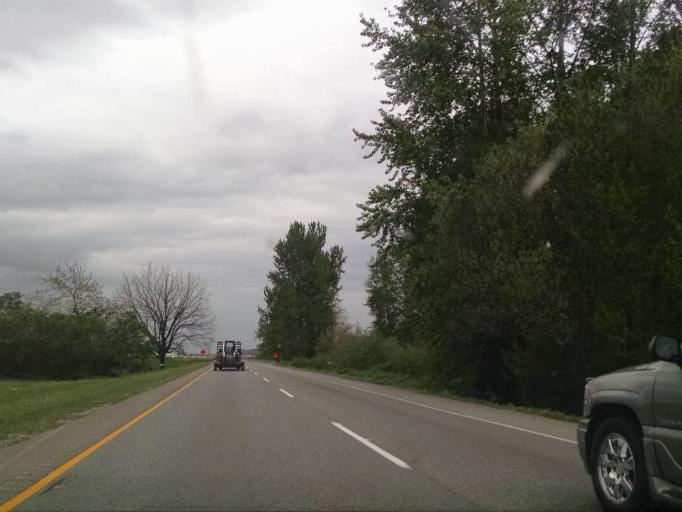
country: CA
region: British Columbia
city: Abbotsford
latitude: 49.0579
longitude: -122.1781
